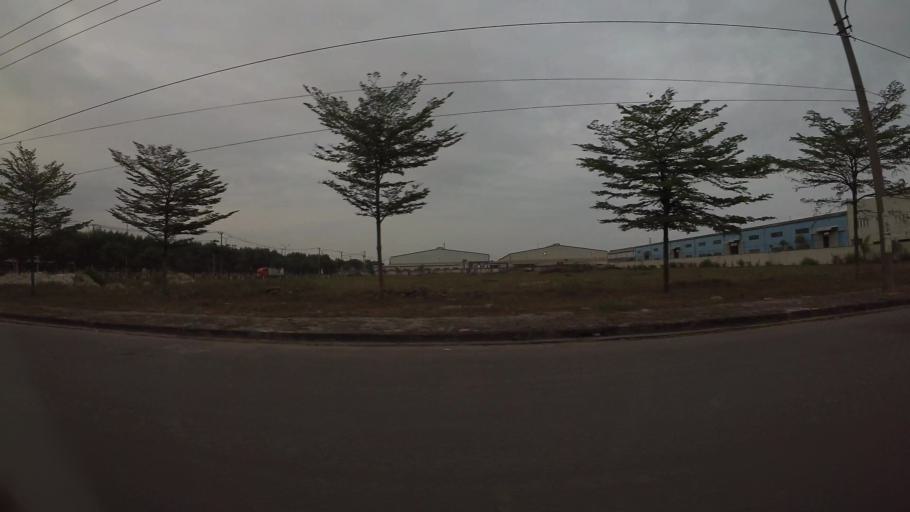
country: VN
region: Da Nang
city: Lien Chieu
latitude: 16.0822
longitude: 108.1184
